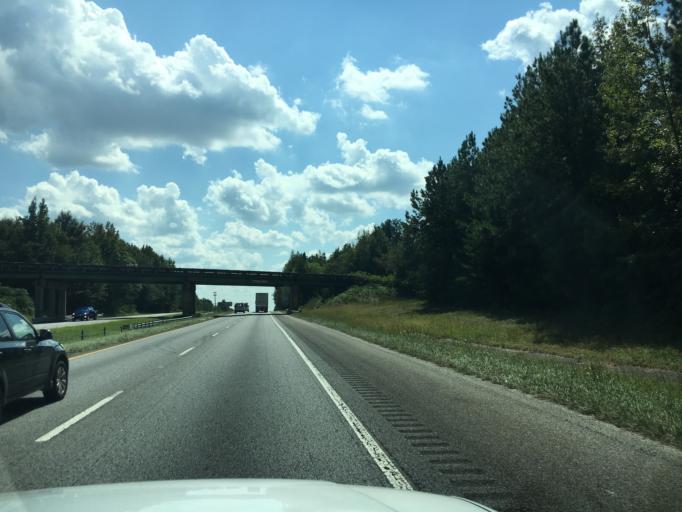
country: US
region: South Carolina
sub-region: Spartanburg County
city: Roebuck
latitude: 34.8991
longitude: -81.9921
